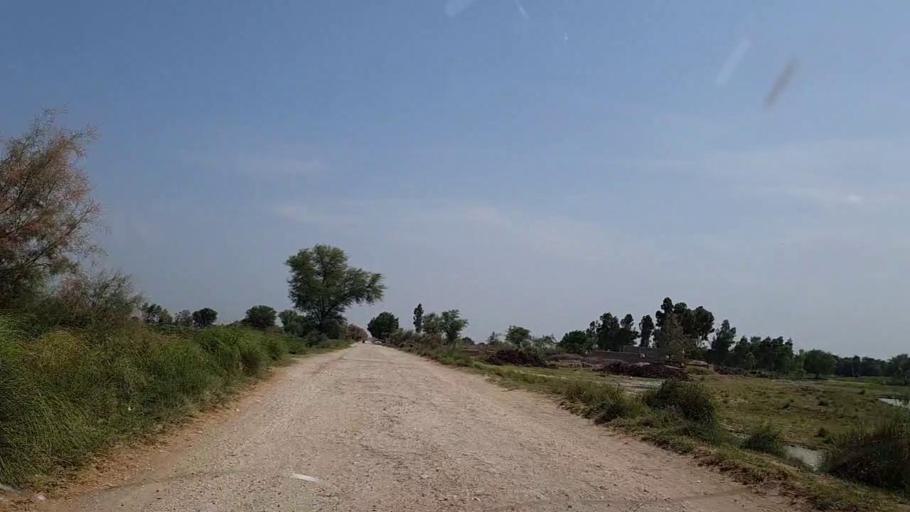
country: PK
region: Sindh
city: Khanpur
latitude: 27.8147
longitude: 69.3069
